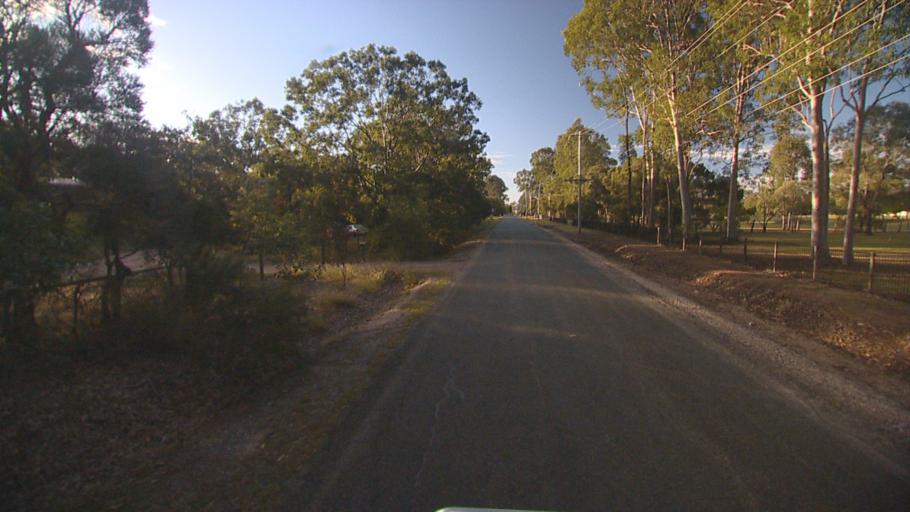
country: AU
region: Queensland
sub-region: Logan
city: Waterford West
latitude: -27.7233
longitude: 153.1417
